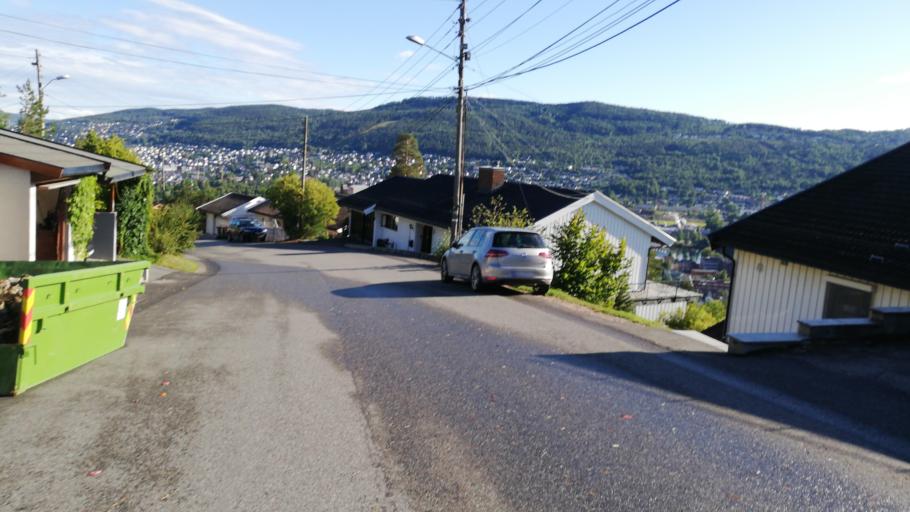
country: NO
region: Buskerud
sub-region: Drammen
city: Drammen
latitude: 59.7554
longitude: 10.1776
